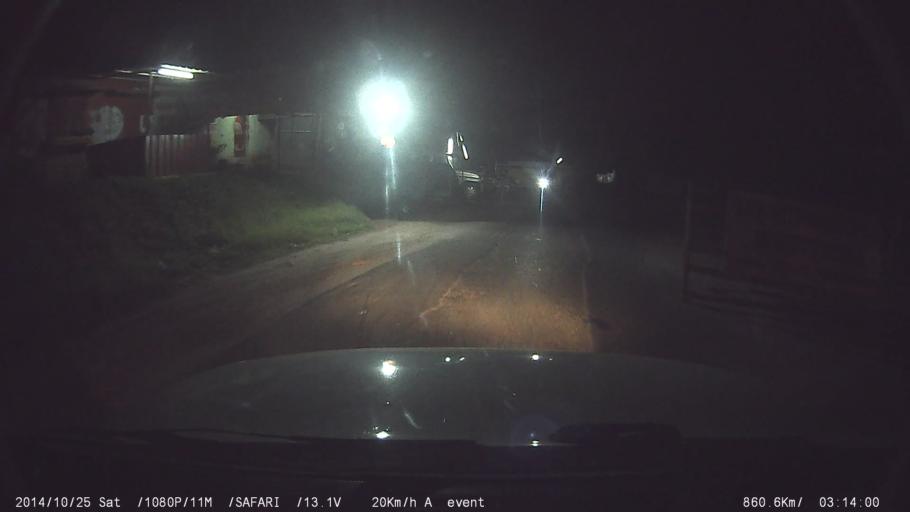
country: IN
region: Tamil Nadu
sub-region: Coimbatore
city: Madukkarai
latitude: 10.8539
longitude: 76.8579
